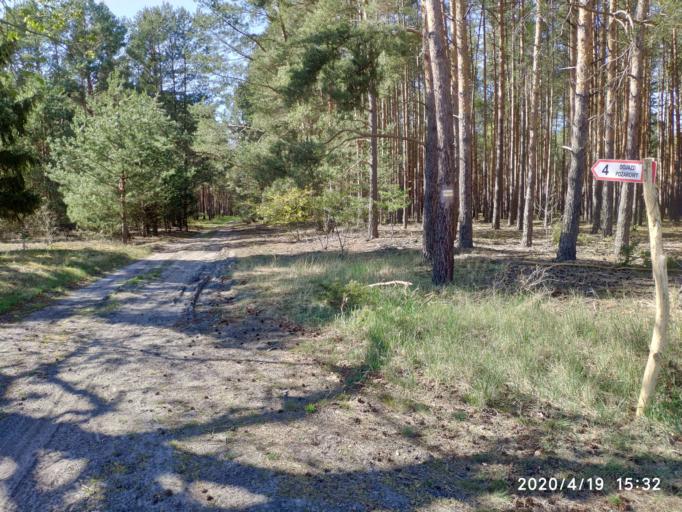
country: PL
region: Lubusz
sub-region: Powiat zielonogorski
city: Zabor
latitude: 51.9733
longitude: 15.6794
